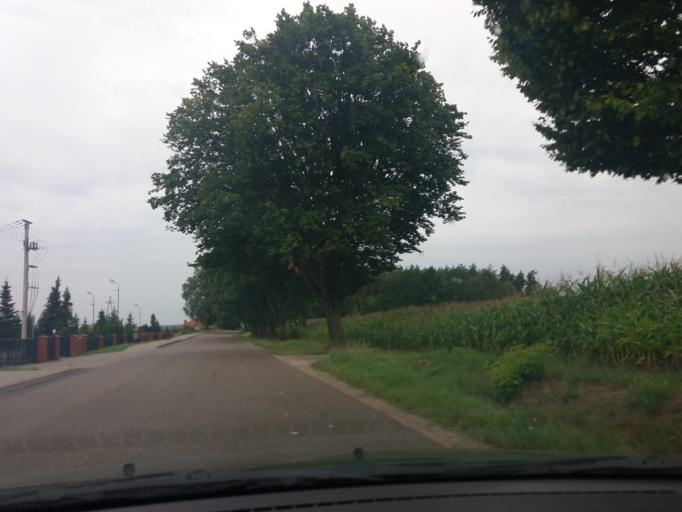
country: PL
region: Masovian Voivodeship
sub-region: Powiat mlawski
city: Wieczfnia Koscielna
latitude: 53.2005
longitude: 20.4891
